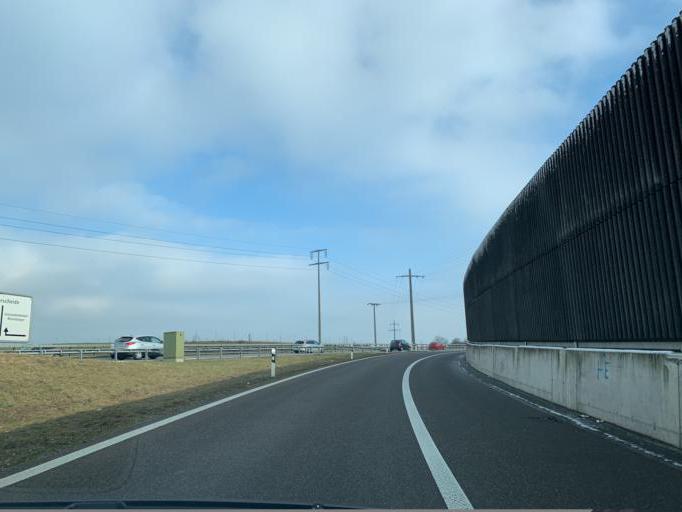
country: CH
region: Zurich
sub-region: Bezirk Winterthur
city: Sulz
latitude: 47.5306
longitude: 8.7765
